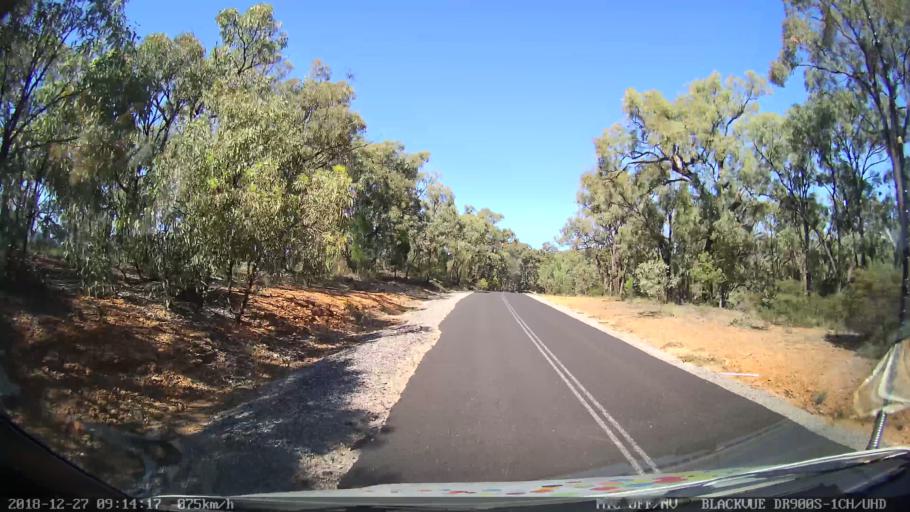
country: AU
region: New South Wales
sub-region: Lithgow
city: Portland
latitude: -33.1377
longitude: 150.0838
